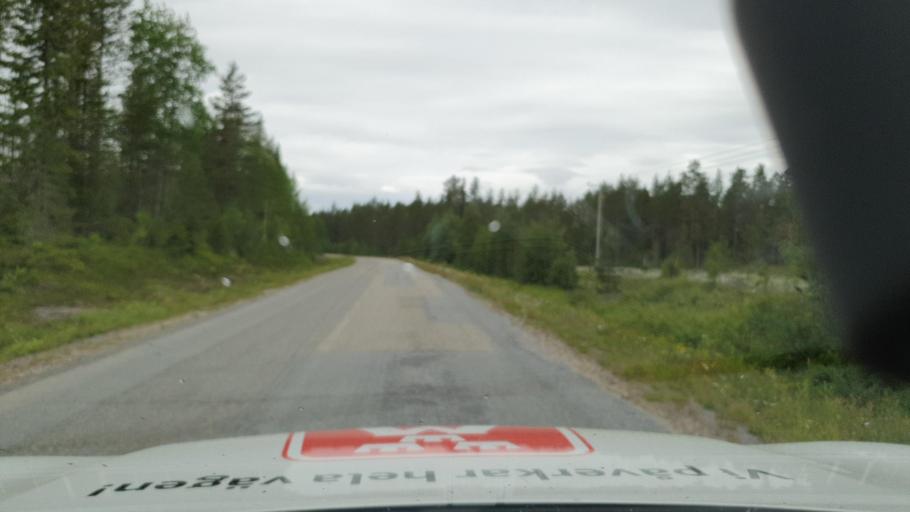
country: SE
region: Vaesterbotten
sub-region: Nordmalings Kommun
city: Nordmaling
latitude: 63.7729
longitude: 19.4161
